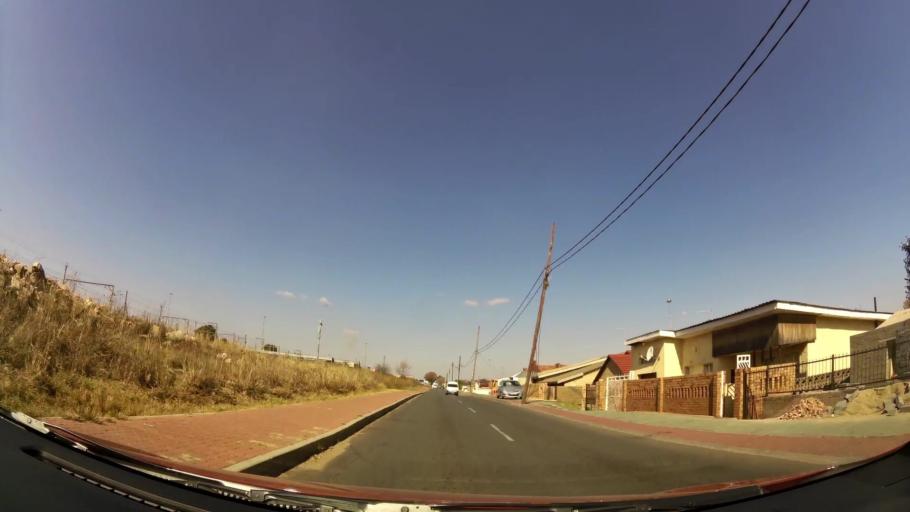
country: ZA
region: Gauteng
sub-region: City of Johannesburg Metropolitan Municipality
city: Soweto
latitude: -26.2308
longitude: 27.8902
